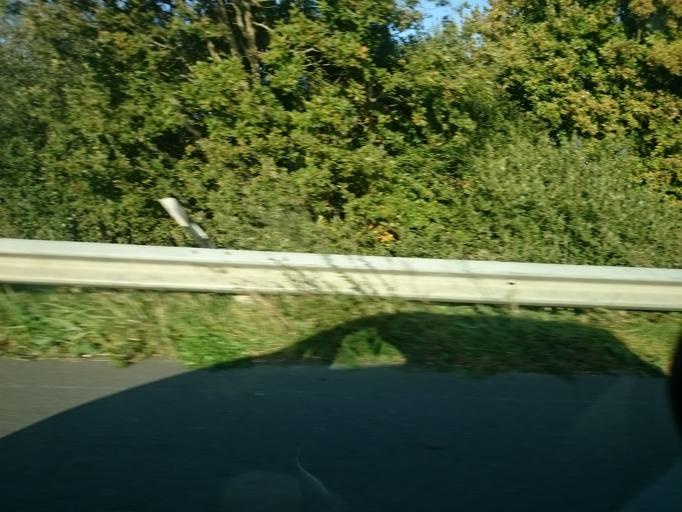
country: FR
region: Pays de la Loire
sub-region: Departement de la Loire-Atlantique
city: Derval
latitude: 47.6566
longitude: -1.6738
